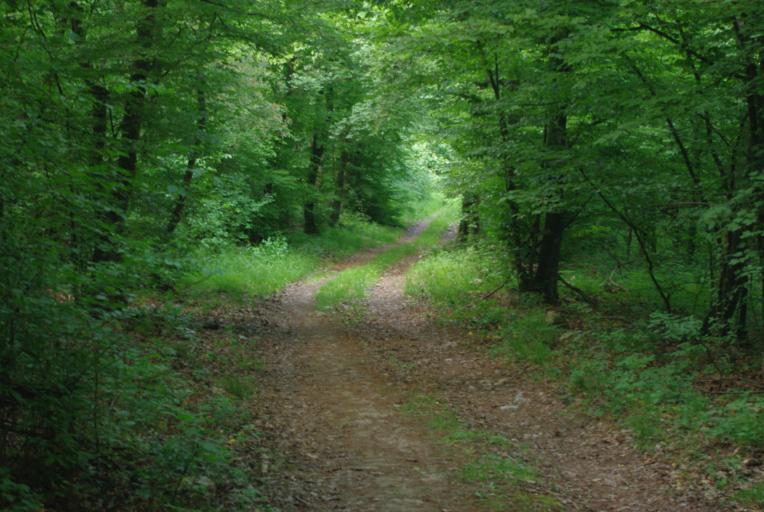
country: HU
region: Pest
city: Pilisszentivan
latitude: 47.5628
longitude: 18.8945
